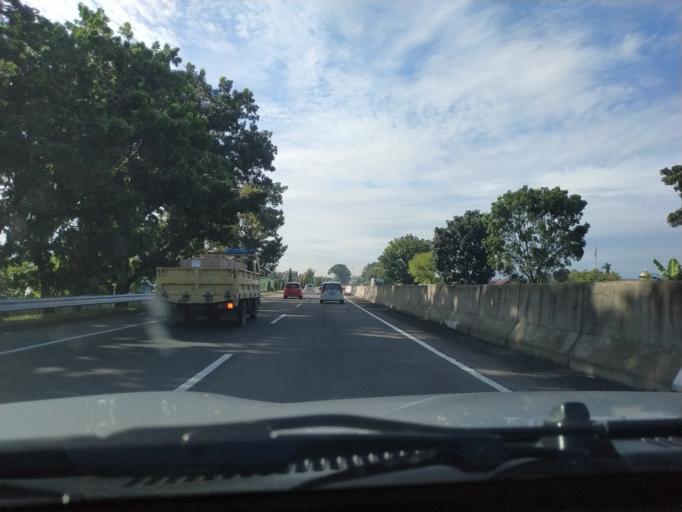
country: ID
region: North Sumatra
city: Medan
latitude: 3.5701
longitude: 98.7258
